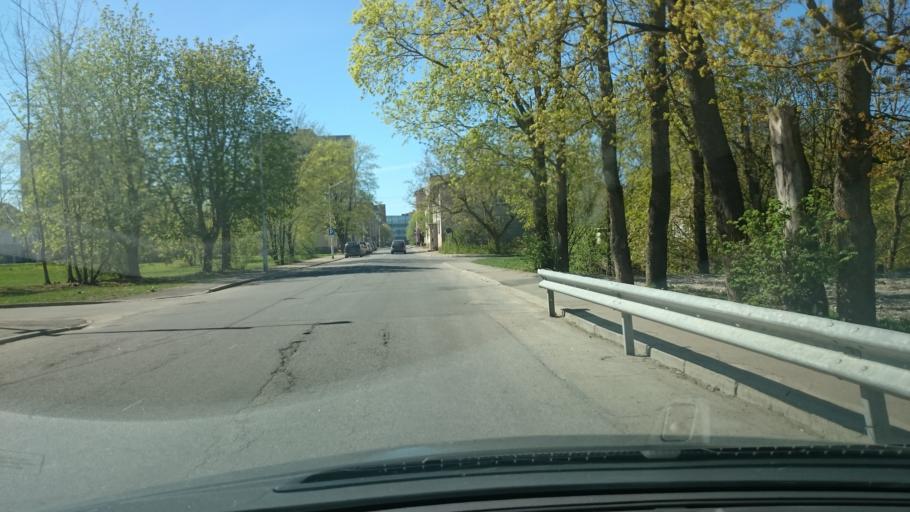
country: EE
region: Ida-Virumaa
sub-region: Narva linn
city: Narva
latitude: 59.3717
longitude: 28.2023
